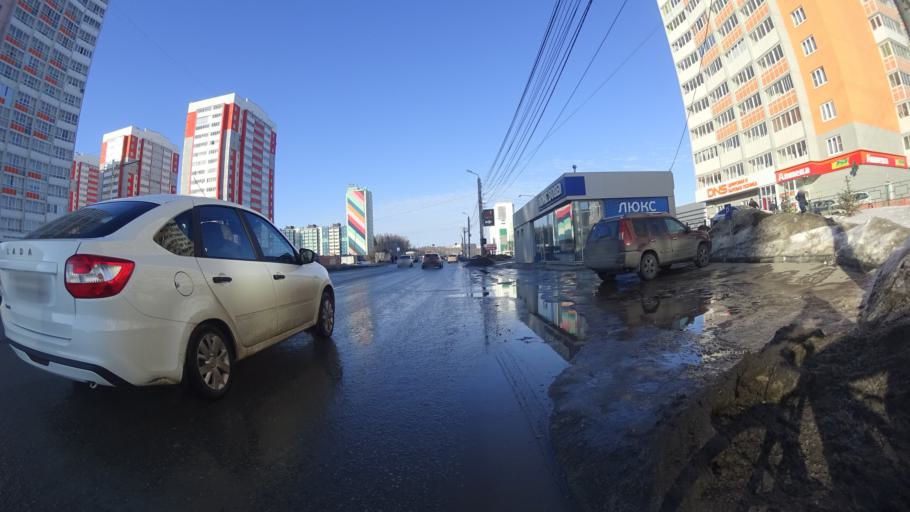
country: RU
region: Chelyabinsk
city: Roshchino
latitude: 55.2083
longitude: 61.2844
